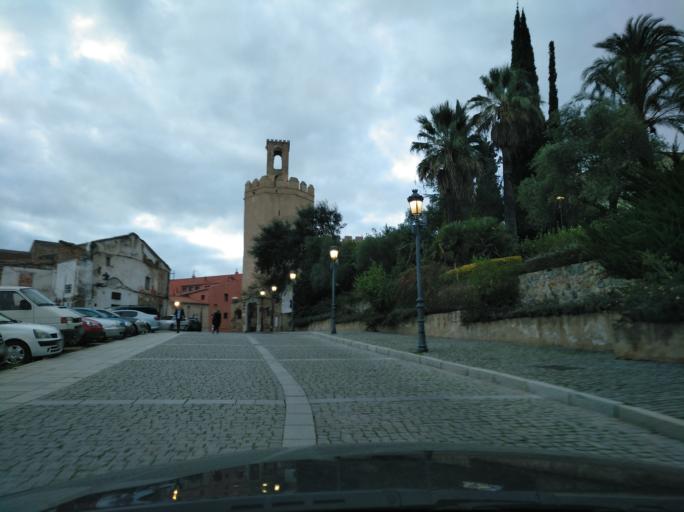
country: ES
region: Extremadura
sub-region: Provincia de Badajoz
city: Badajoz
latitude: 38.8812
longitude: -6.9665
